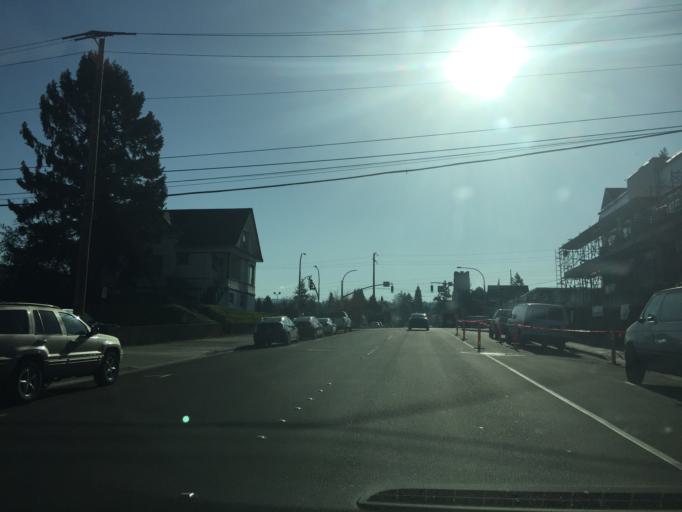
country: US
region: Washington
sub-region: Whatcom County
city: Bellingham
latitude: 48.7493
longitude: -122.4753
